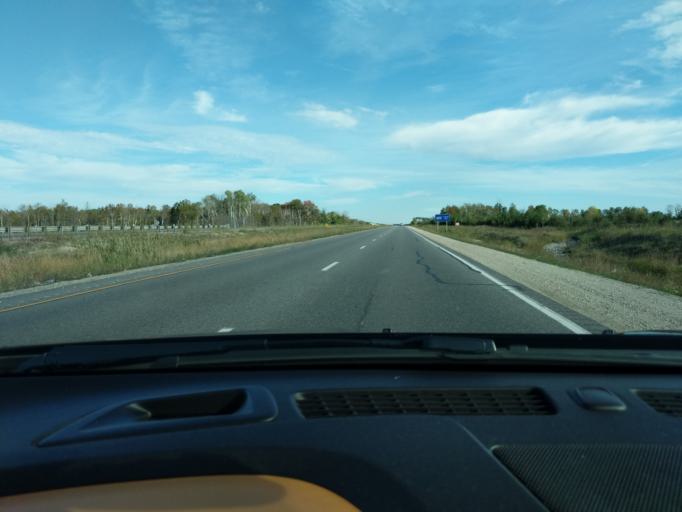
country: CA
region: Ontario
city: Collingwood
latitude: 44.4815
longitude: -80.1686
